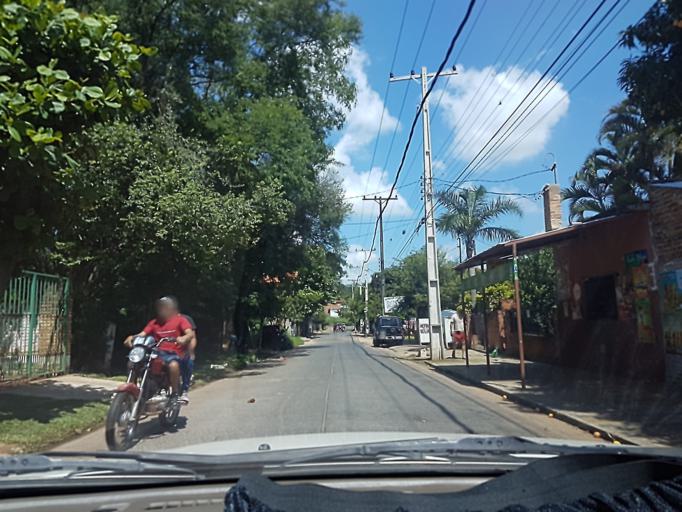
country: PY
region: Central
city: San Lorenzo
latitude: -25.2628
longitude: -57.4960
